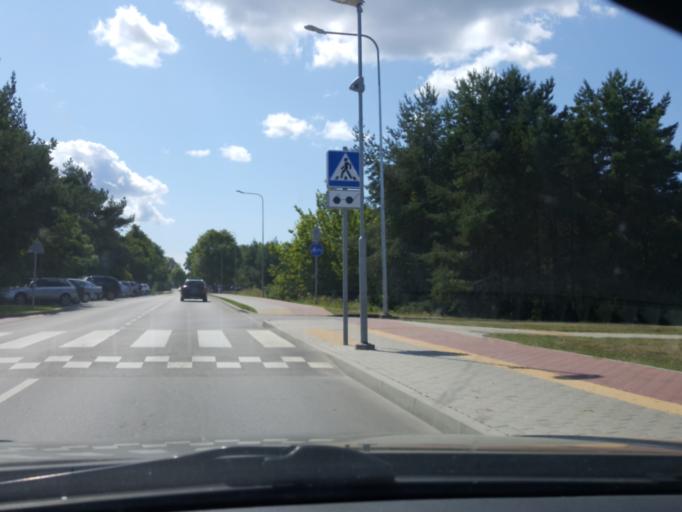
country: LT
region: Klaipedos apskritis
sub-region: Klaipeda
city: Palanga
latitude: 55.9351
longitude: 21.0773
